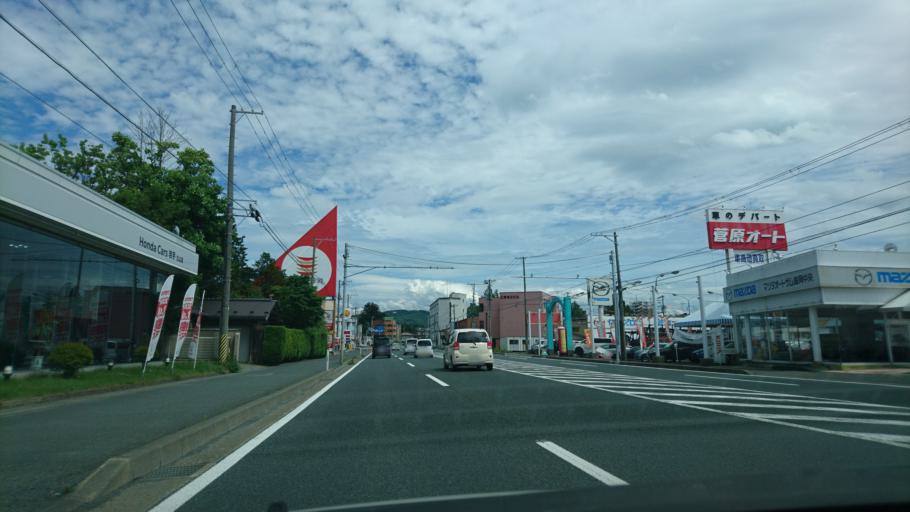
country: JP
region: Iwate
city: Morioka-shi
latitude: 39.7175
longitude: 141.1450
